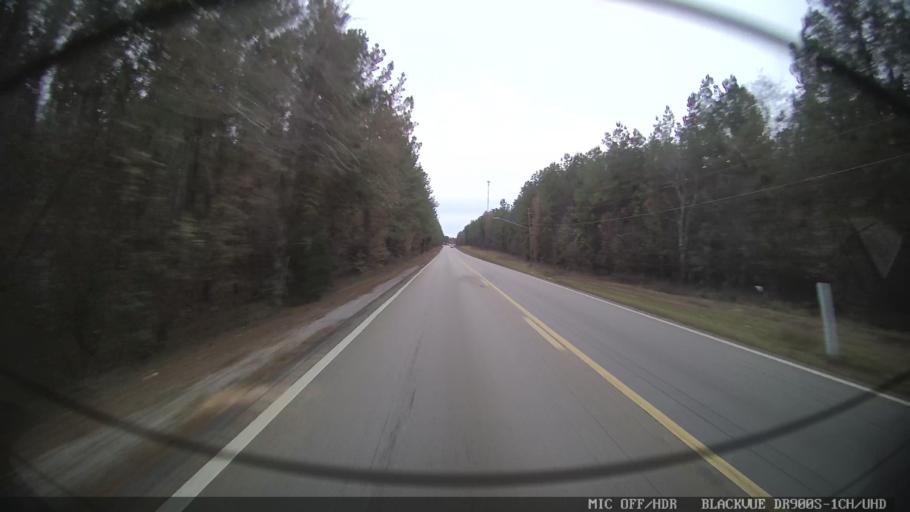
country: US
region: Mississippi
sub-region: Clarke County
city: Stonewall
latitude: 32.0508
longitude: -88.8959
